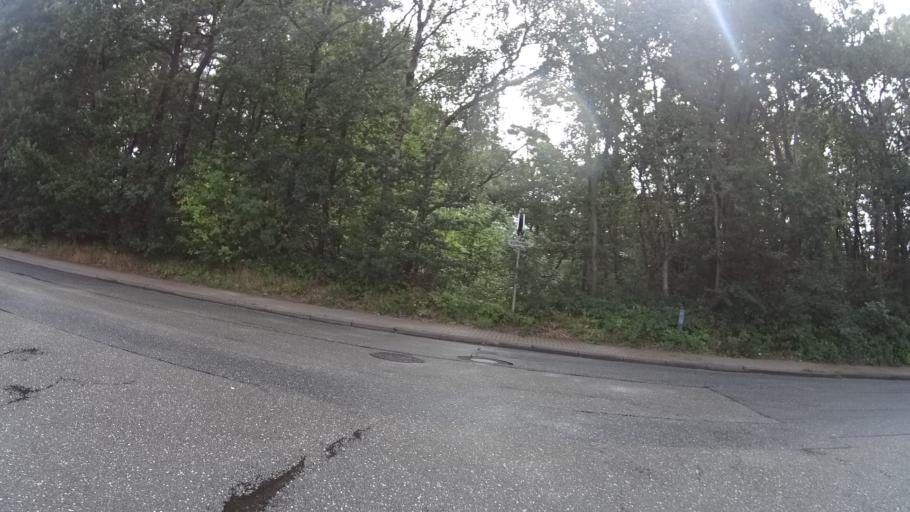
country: DE
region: Schleswig-Holstein
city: Henstedt-Ulzburg
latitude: 53.7642
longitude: 9.9881
